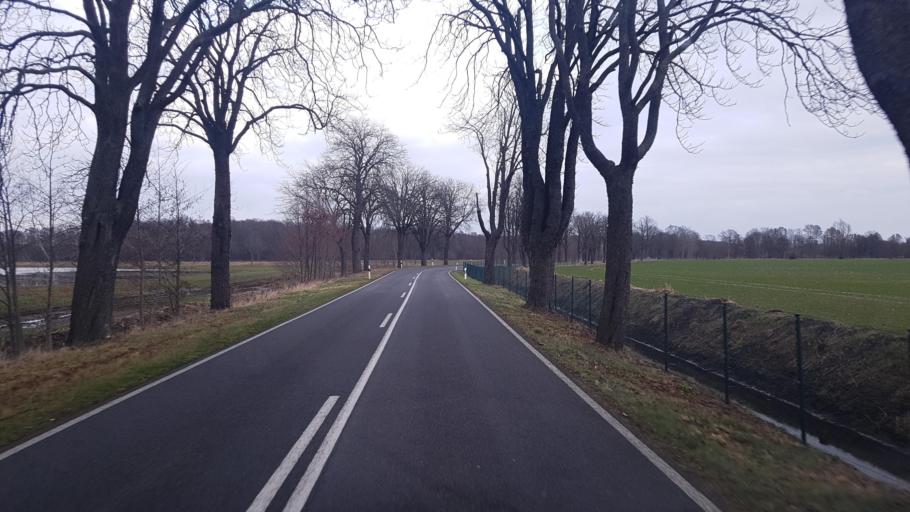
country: DE
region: Brandenburg
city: Drahnsdorf
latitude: 51.9239
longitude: 13.6102
